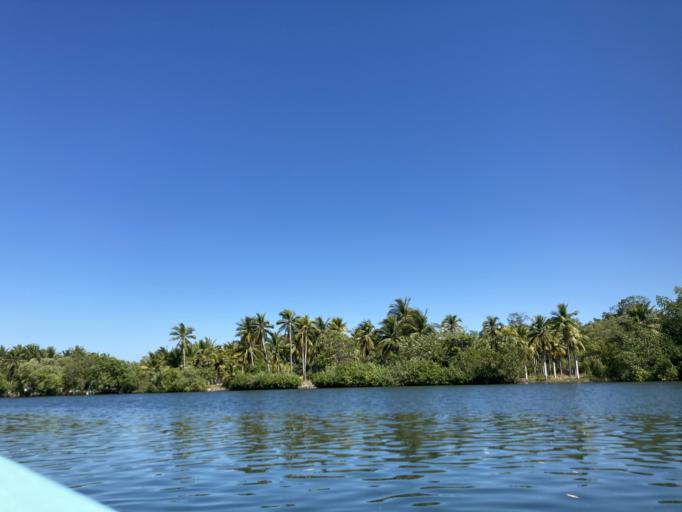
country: GT
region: Jutiapa
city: Pasaco
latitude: 13.8074
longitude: -90.2703
